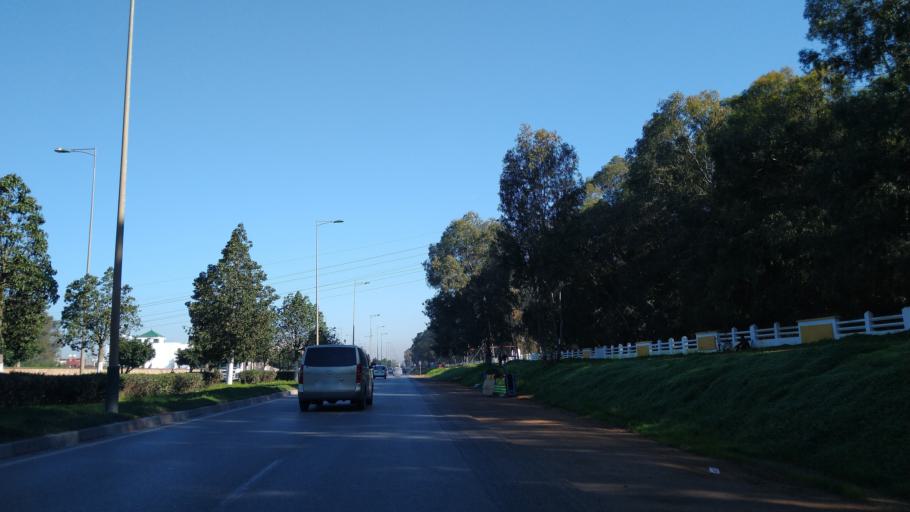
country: MA
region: Rabat-Sale-Zemmour-Zaer
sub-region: Skhirate-Temara
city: Temara
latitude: 33.9325
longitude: -6.8876
